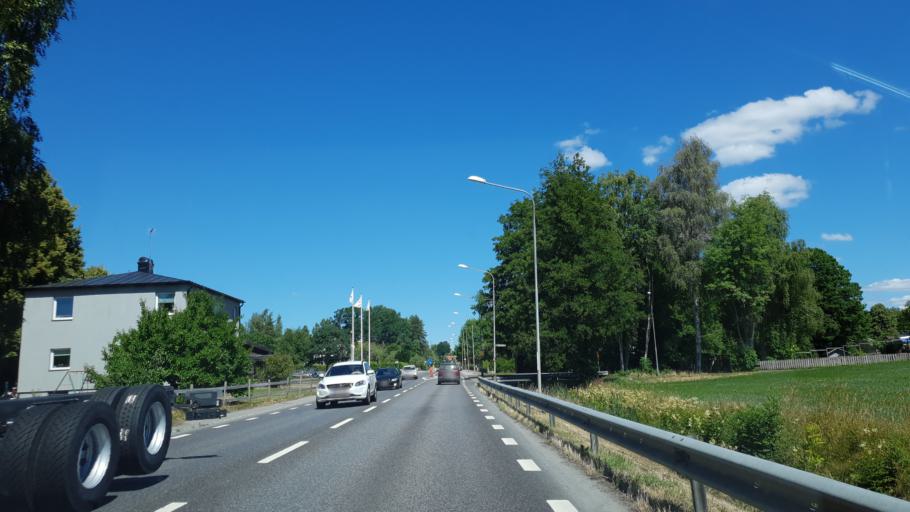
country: SE
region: Joenkoeping
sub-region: Varnamo Kommun
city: Bor
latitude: 57.1065
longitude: 14.1700
